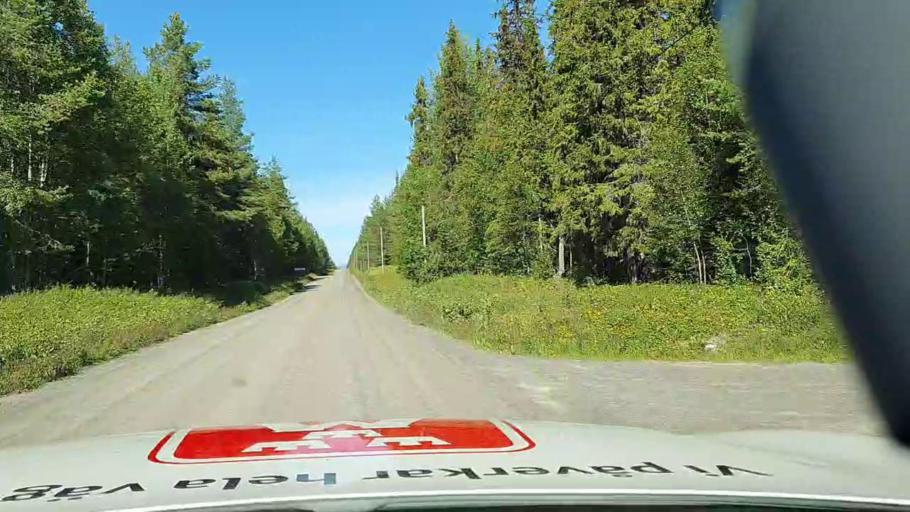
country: SE
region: Jaemtland
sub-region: Krokoms Kommun
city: Krokom
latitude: 63.6848
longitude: 14.6039
